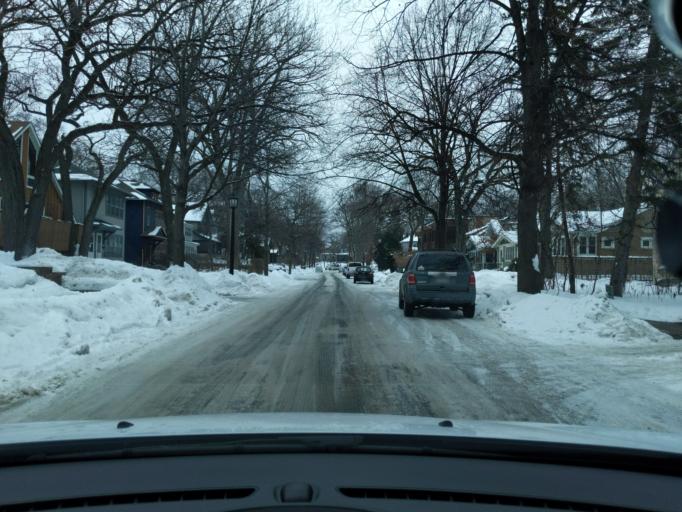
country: US
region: Minnesota
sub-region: Ramsey County
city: Lauderdale
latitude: 44.9655
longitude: -93.2126
